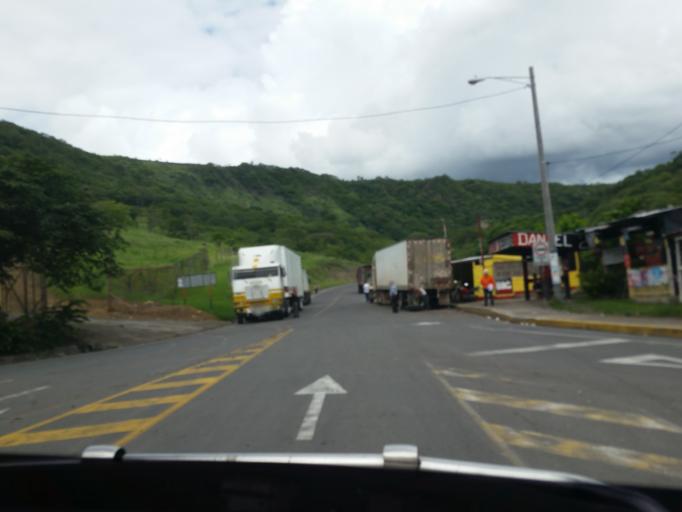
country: NI
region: Matagalpa
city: Matagalpa
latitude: 12.9217
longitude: -86.0097
